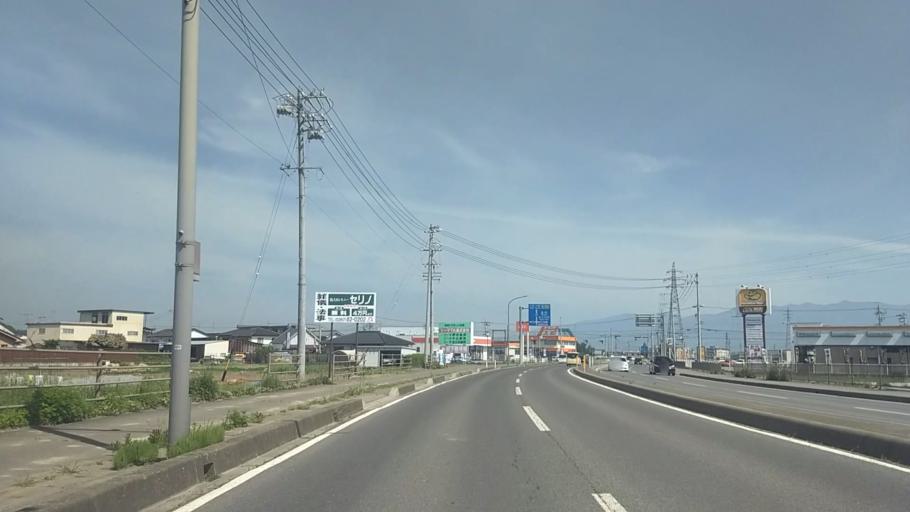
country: JP
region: Nagano
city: Saku
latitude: 36.2232
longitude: 138.4576
